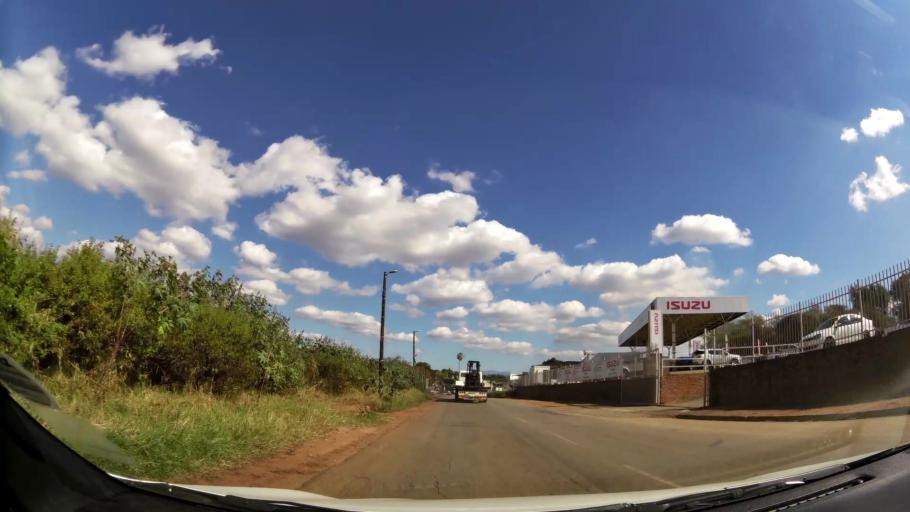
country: ZA
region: Limpopo
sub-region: Mopani District Municipality
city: Tzaneen
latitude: -23.8224
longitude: 30.1608
